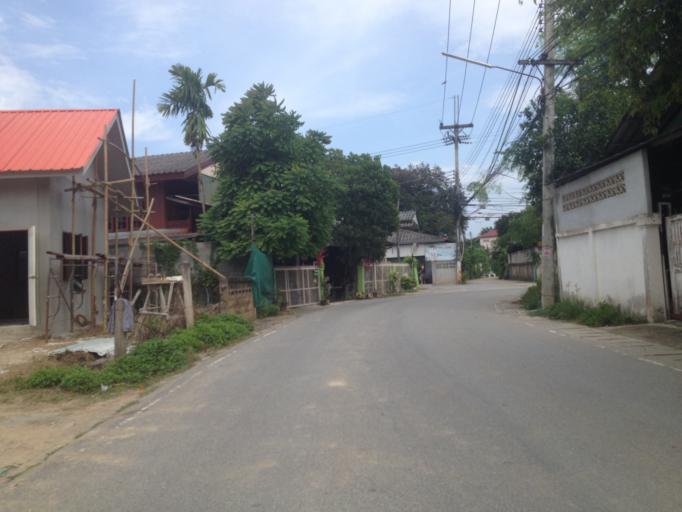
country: TH
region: Chiang Mai
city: Hang Dong
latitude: 18.6830
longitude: 98.9519
